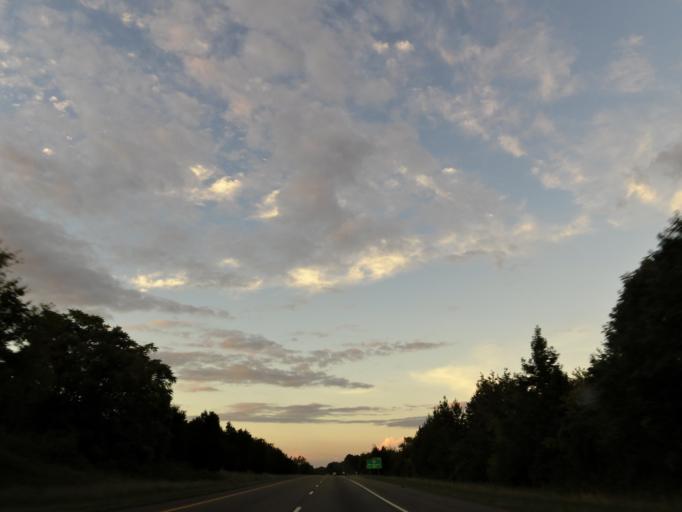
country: US
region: Tennessee
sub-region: Monroe County
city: Sweetwater
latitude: 35.6875
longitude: -84.4350
